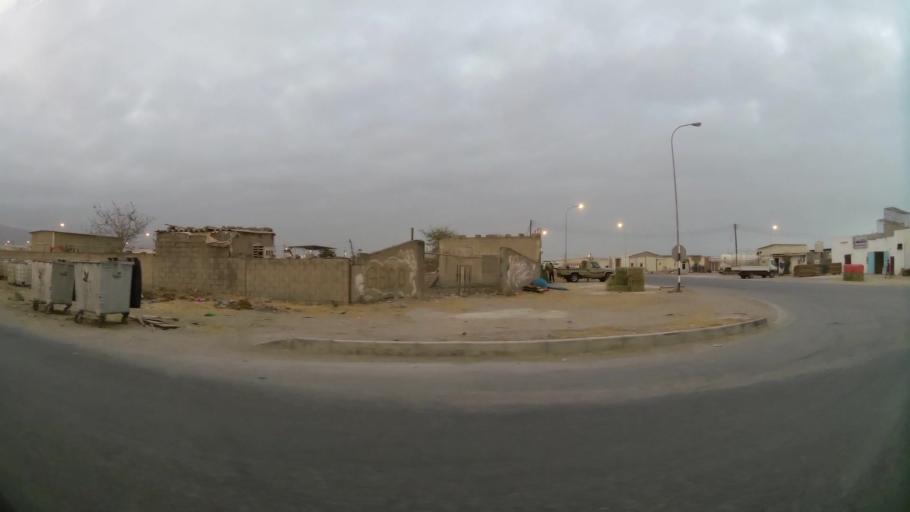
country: OM
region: Zufar
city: Salalah
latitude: 17.0251
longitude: 54.0345
